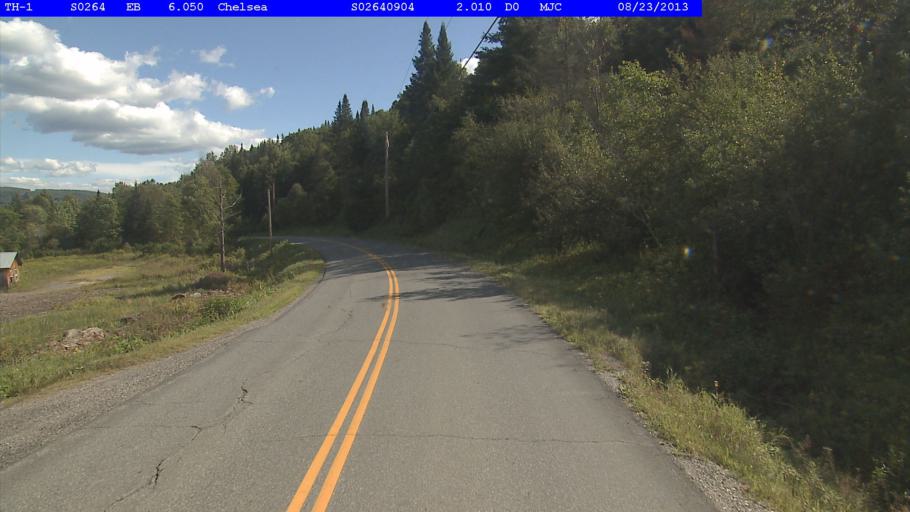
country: US
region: Vermont
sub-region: Orange County
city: Chelsea
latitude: 43.9678
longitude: -72.4780
